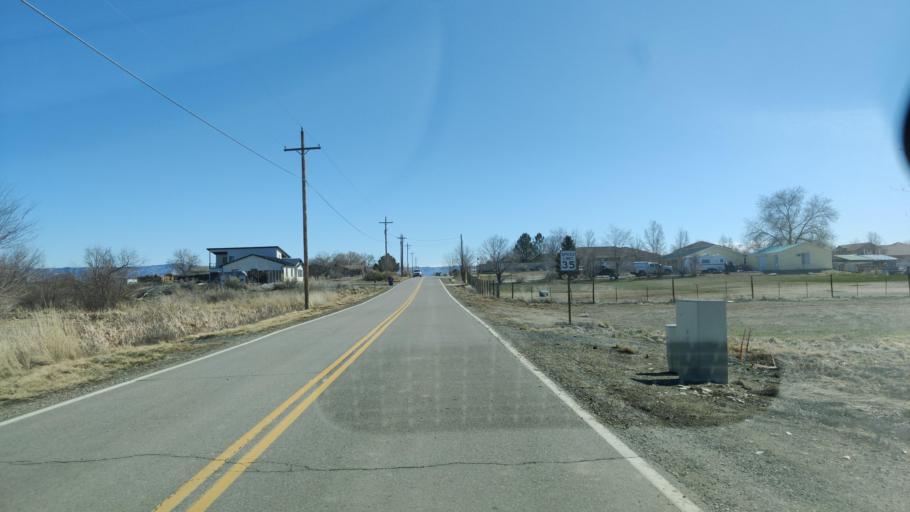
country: US
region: Colorado
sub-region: Mesa County
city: Fruita
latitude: 39.1788
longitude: -108.7191
